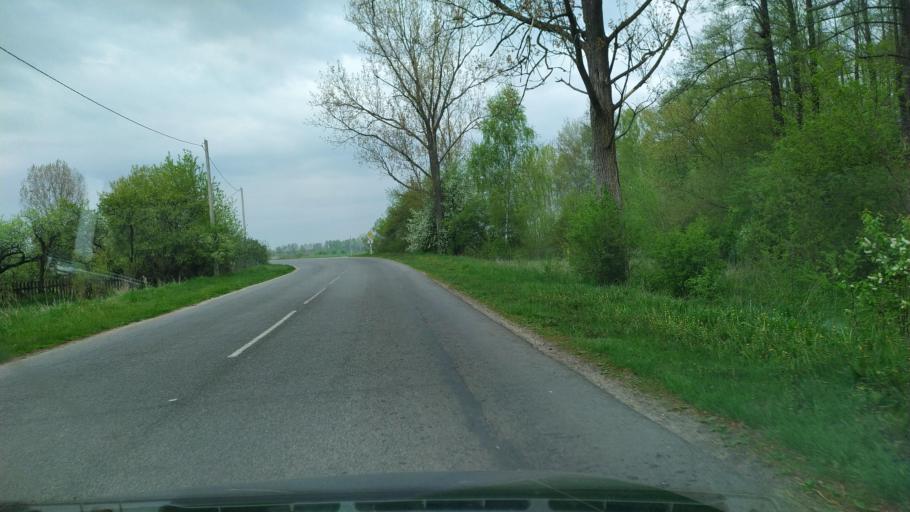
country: BY
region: Brest
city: Zhabinka
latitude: 52.1558
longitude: 24.0971
